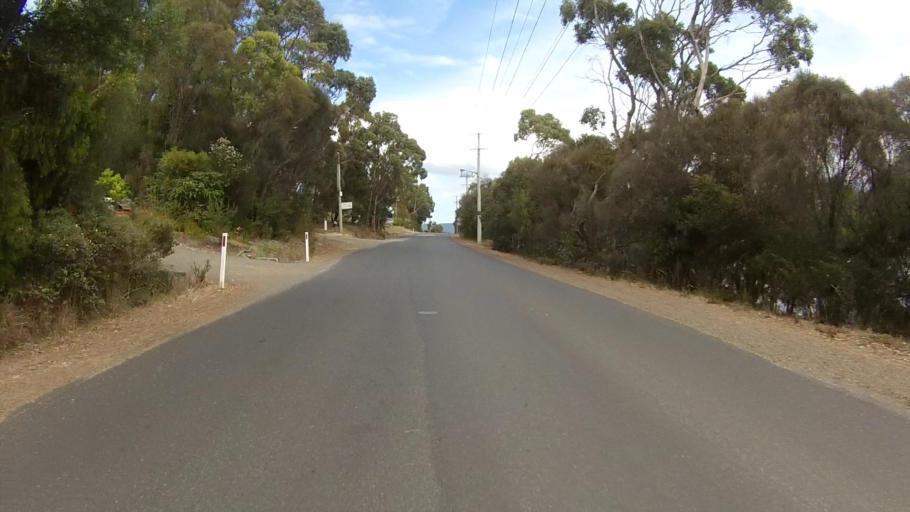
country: AU
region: Tasmania
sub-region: Kingborough
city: Margate
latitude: -43.0217
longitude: 147.2915
